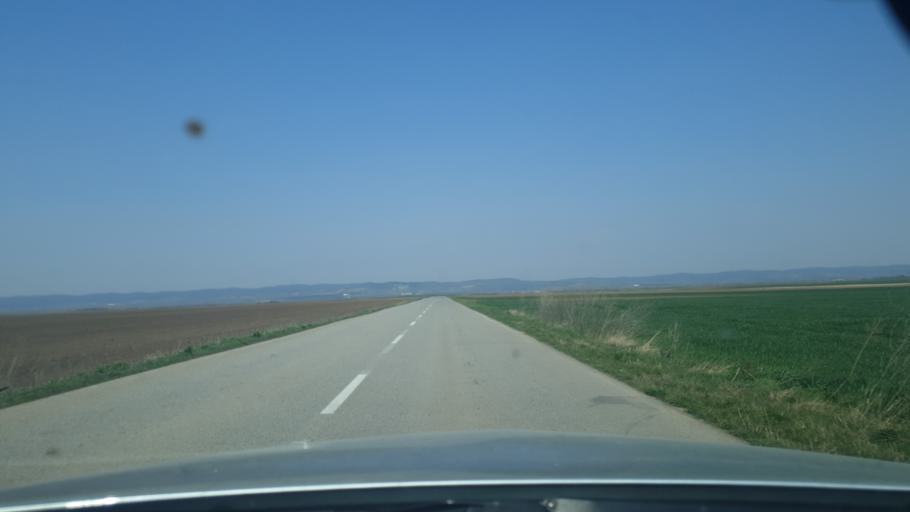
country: RS
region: Autonomna Pokrajina Vojvodina
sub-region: Sremski Okrug
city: Ruma
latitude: 45.0264
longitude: 19.7627
